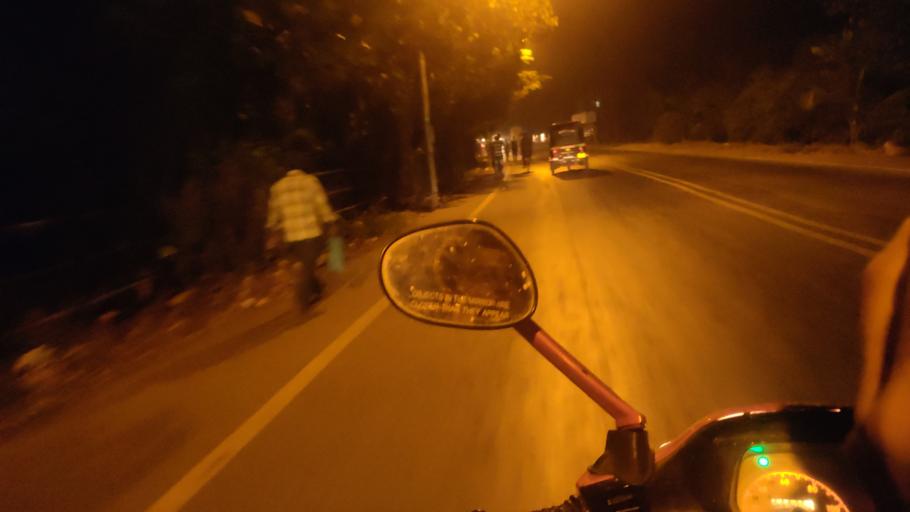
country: IN
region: Maharashtra
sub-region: Thane
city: Bhayandar
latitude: 19.2993
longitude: 72.8375
